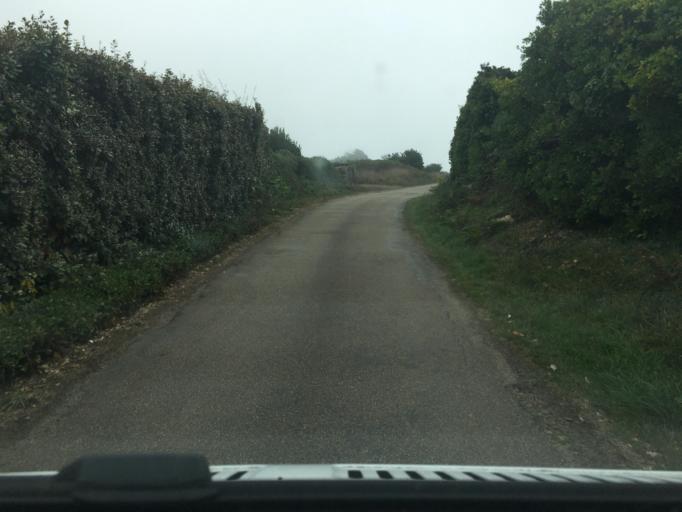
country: FR
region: Brittany
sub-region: Departement du Finistere
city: Plogoff
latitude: 48.0316
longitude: -4.6969
